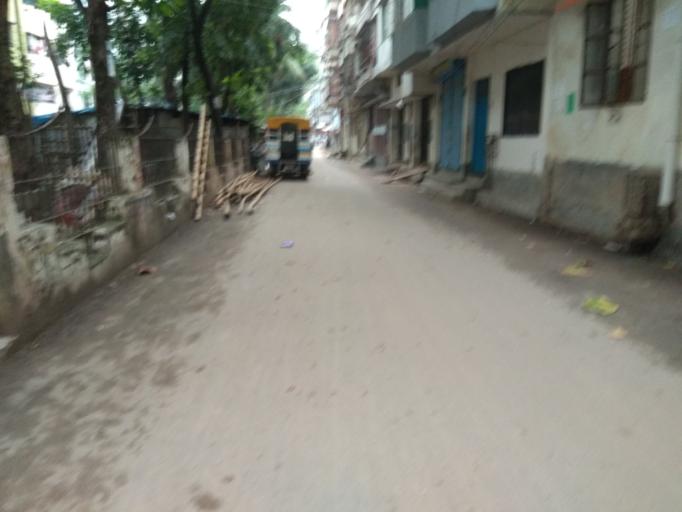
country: BD
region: Dhaka
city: Tungi
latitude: 23.8253
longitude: 90.3747
